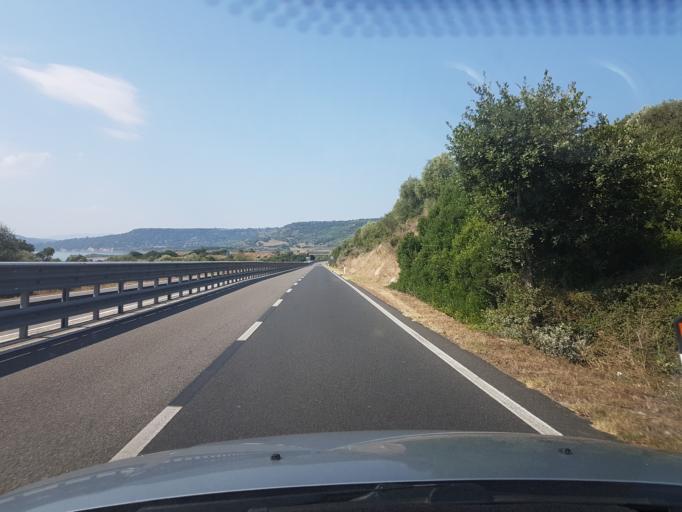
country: IT
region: Sardinia
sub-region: Provincia di Oristano
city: Sedilo
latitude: 40.1553
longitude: 8.9048
